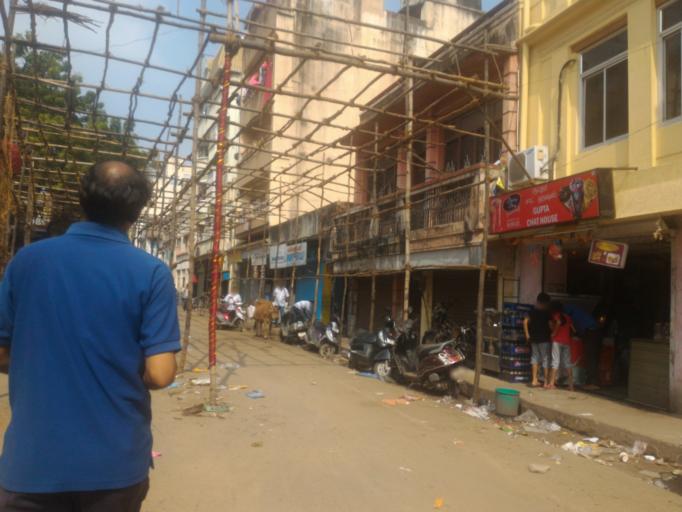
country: IN
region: Tamil Nadu
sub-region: Chennai
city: George Town
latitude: 13.0960
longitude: 80.2806
